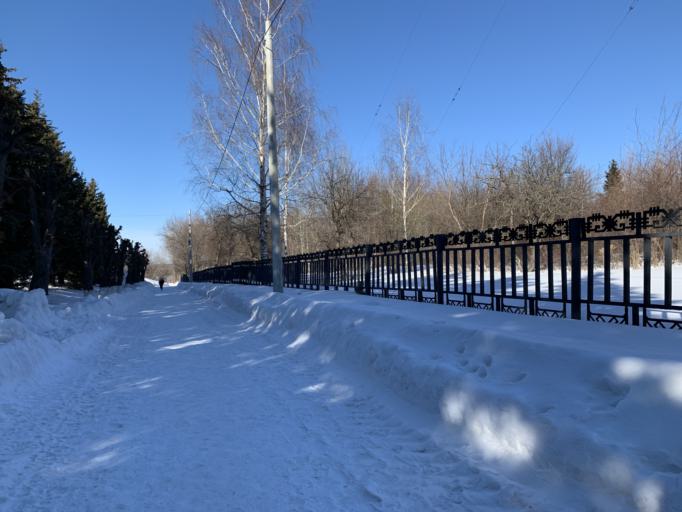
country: RU
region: Chuvashia
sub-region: Cheboksarskiy Rayon
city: Cheboksary
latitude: 56.1477
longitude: 47.2700
